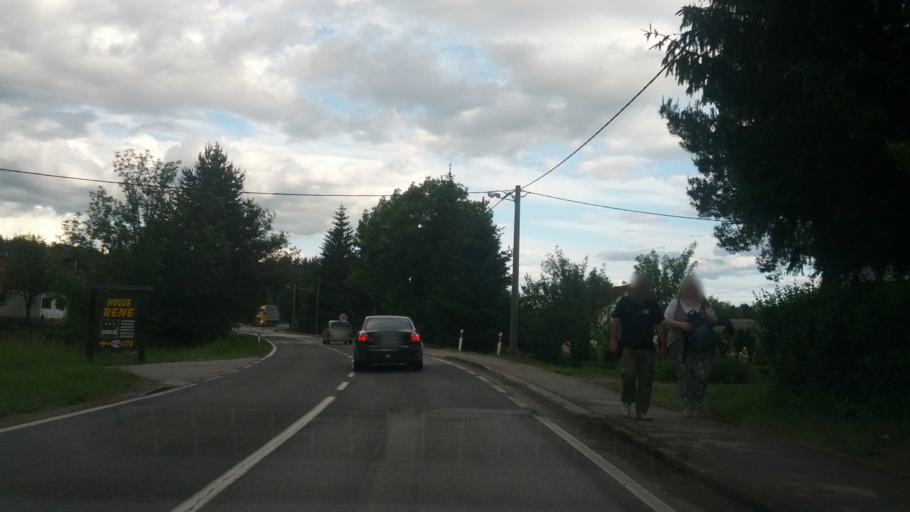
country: HR
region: Licko-Senjska
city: Jezerce
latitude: 44.9701
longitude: 15.6498
